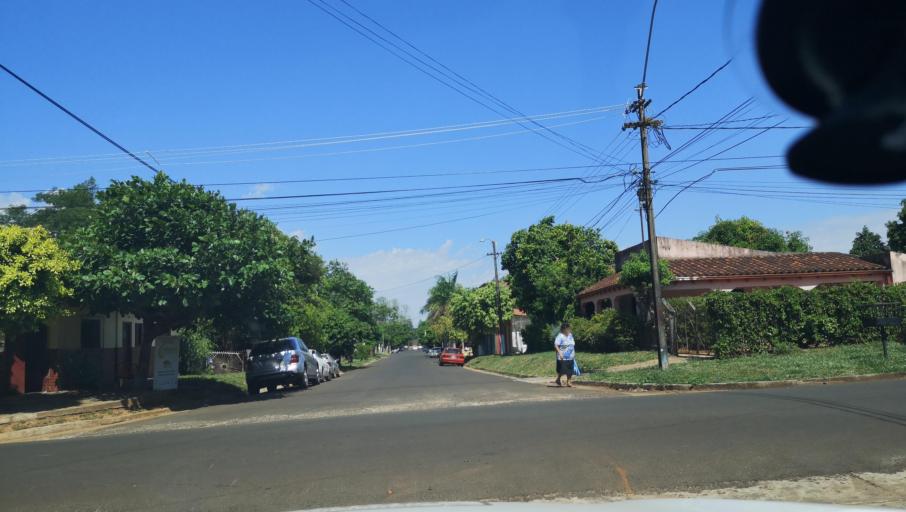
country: PY
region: Itapua
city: Carmen del Parana
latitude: -27.1579
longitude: -56.2367
